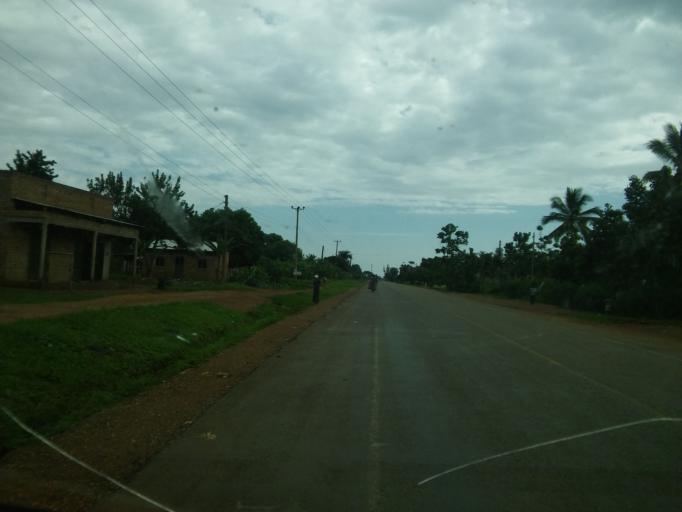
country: UG
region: Eastern Region
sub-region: Mbale District
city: Mbale
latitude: 1.1263
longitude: 34.1680
